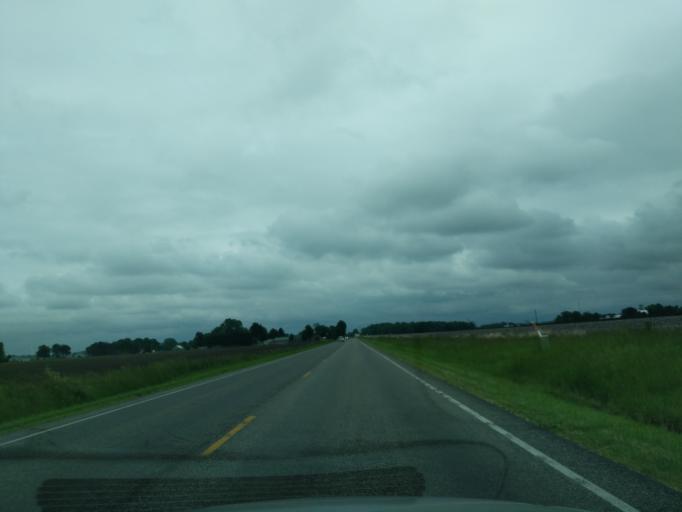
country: US
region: Indiana
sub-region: Madison County
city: Elwood
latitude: 40.2777
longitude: -85.8866
